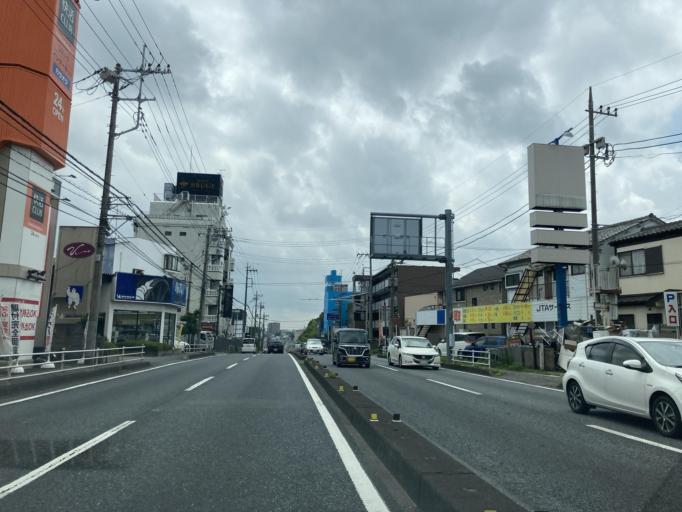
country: JP
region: Saitama
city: Asaka
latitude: 35.7952
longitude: 139.5726
